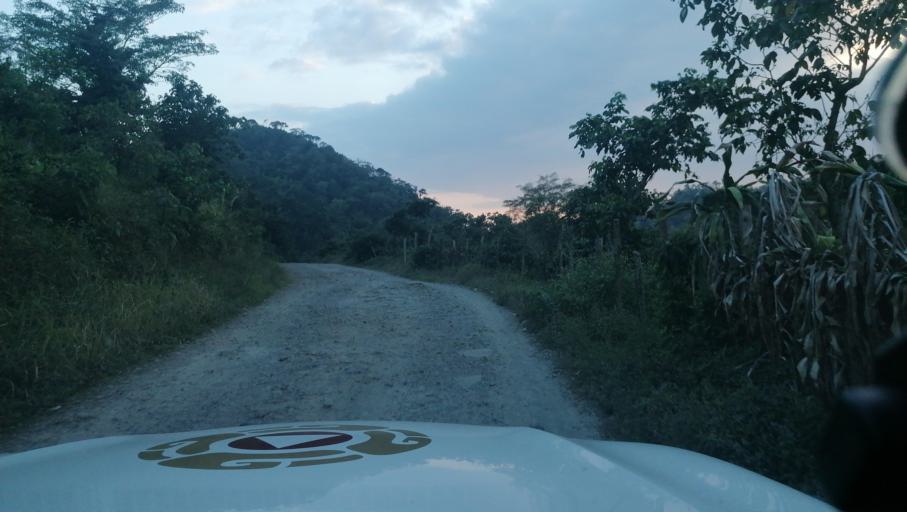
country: MX
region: Chiapas
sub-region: Cacahoatan
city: Benito Juarez
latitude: 15.0681
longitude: -92.2340
